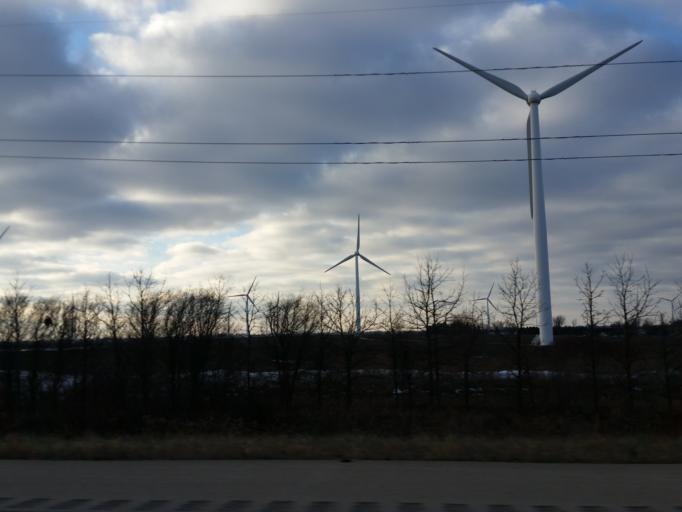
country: US
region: Illinois
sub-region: LaSalle County
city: Mendota
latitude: 41.6637
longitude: -89.0593
